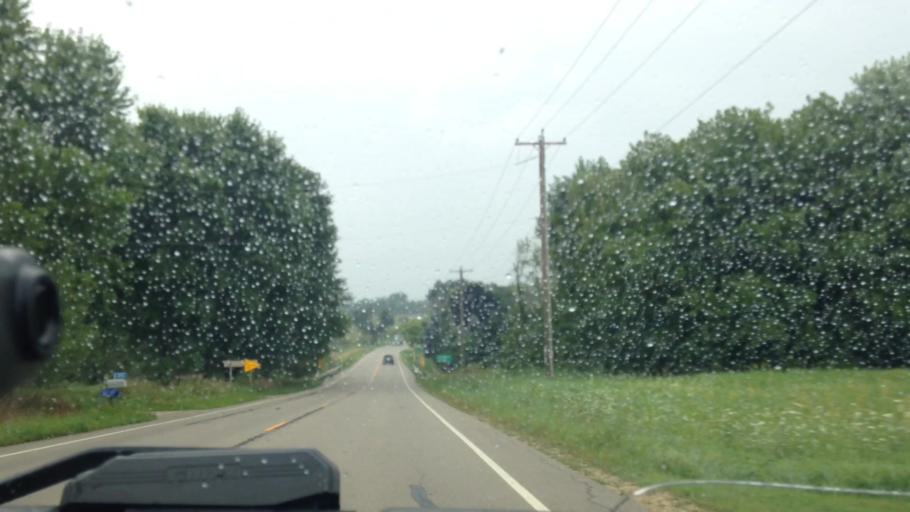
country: US
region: Wisconsin
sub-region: Washington County
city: Hartford
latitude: 43.4018
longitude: -88.3649
